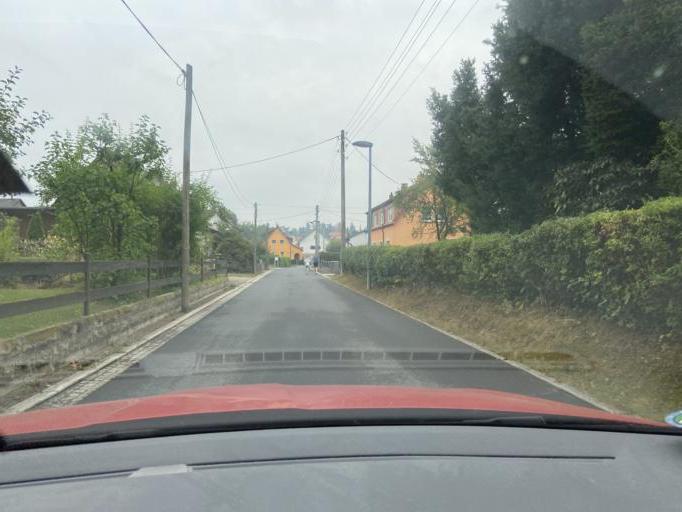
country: DE
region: Saxony
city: Wilsdruff
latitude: 51.0328
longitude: 13.5439
